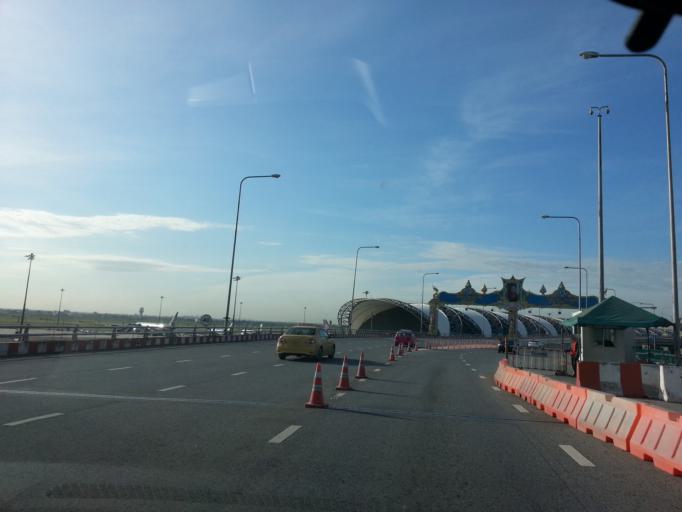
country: TH
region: Bangkok
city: Lat Krabang
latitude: 13.6962
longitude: 100.7542
